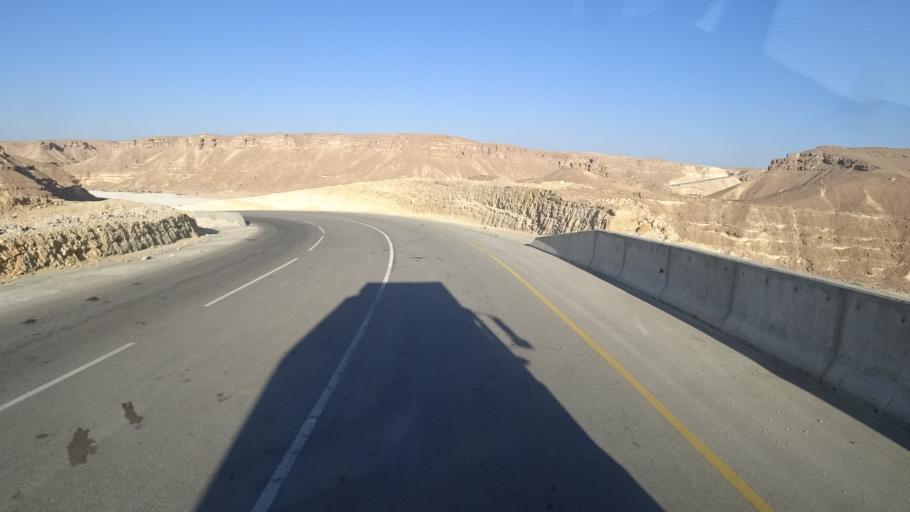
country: YE
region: Al Mahrah
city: Hawf
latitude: 17.0943
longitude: 53.0455
